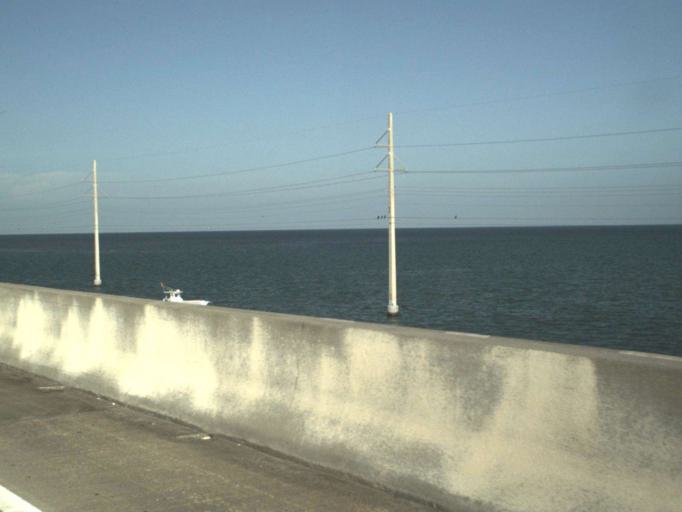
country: US
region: Florida
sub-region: Monroe County
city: Marathon
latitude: 24.8013
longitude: -80.8559
